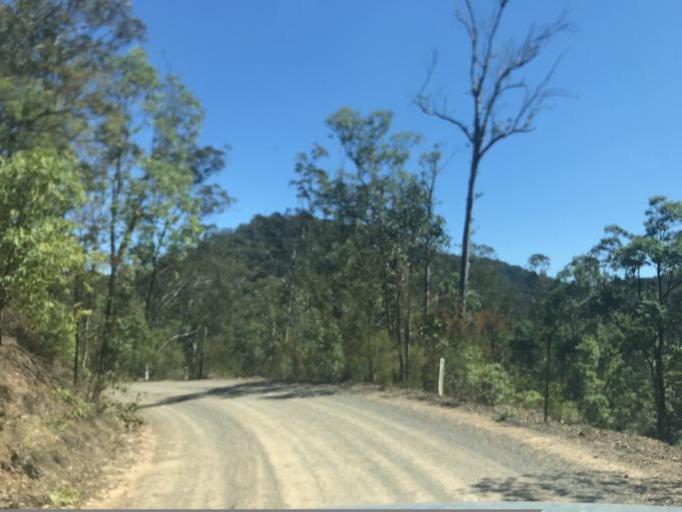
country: AU
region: New South Wales
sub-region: Wyong Shire
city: Little Jilliby
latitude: -33.1614
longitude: 151.0718
